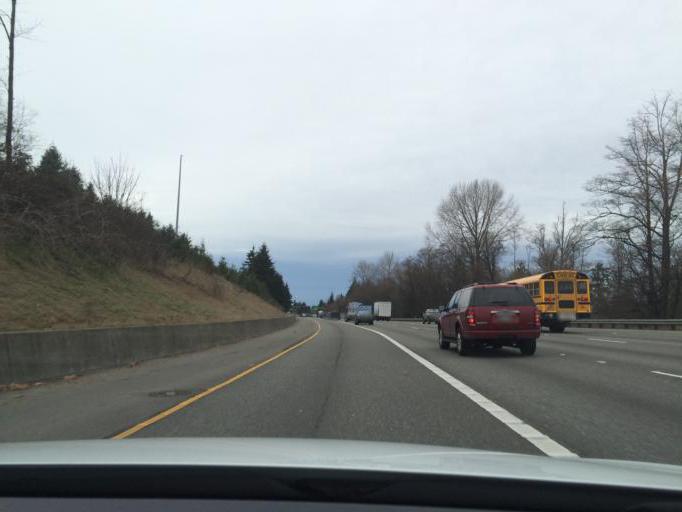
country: US
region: Washington
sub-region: Snohomish County
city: Everett
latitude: 47.9423
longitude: -122.1966
